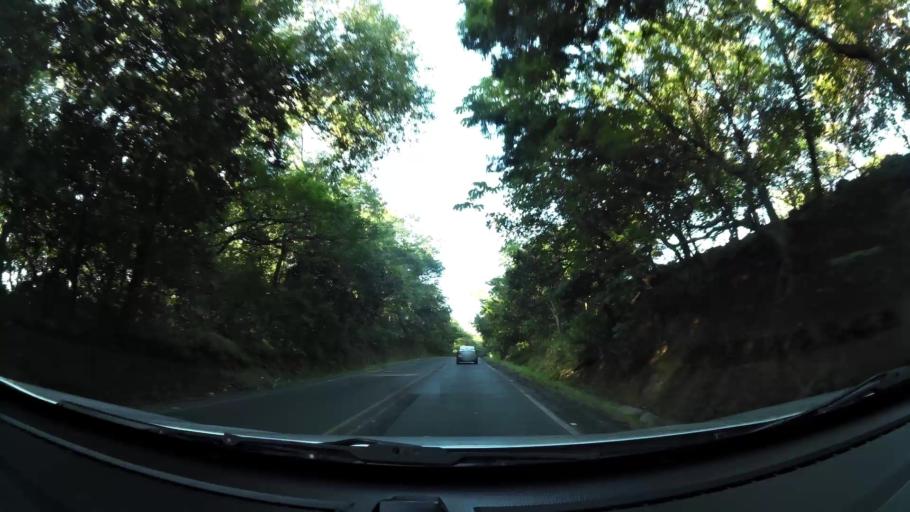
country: CR
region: Puntarenas
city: Miramar
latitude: 10.0971
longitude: -84.8145
